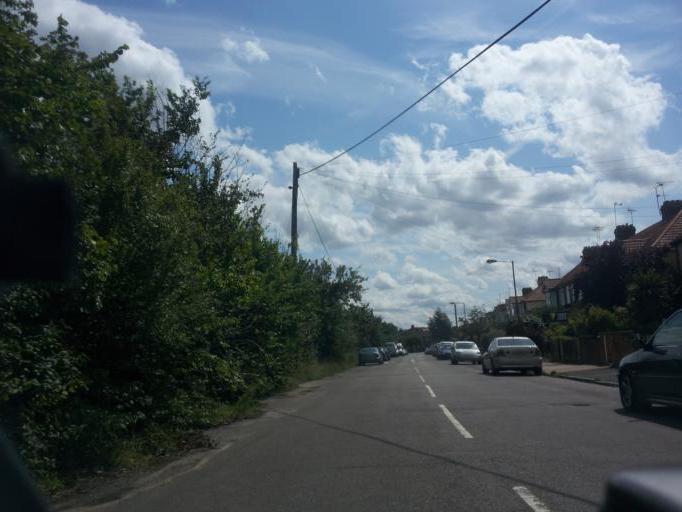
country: GB
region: England
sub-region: Kent
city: Rainham
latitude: 51.3852
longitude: 0.5833
